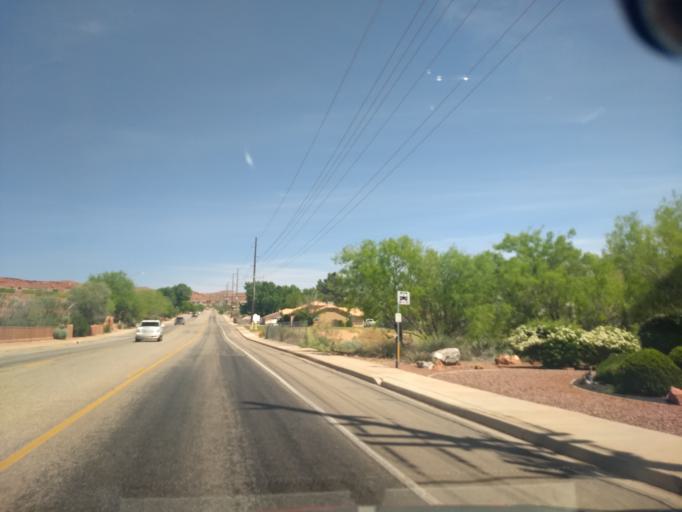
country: US
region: Utah
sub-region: Washington County
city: Santa Clara
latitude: 37.1429
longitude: -113.6349
